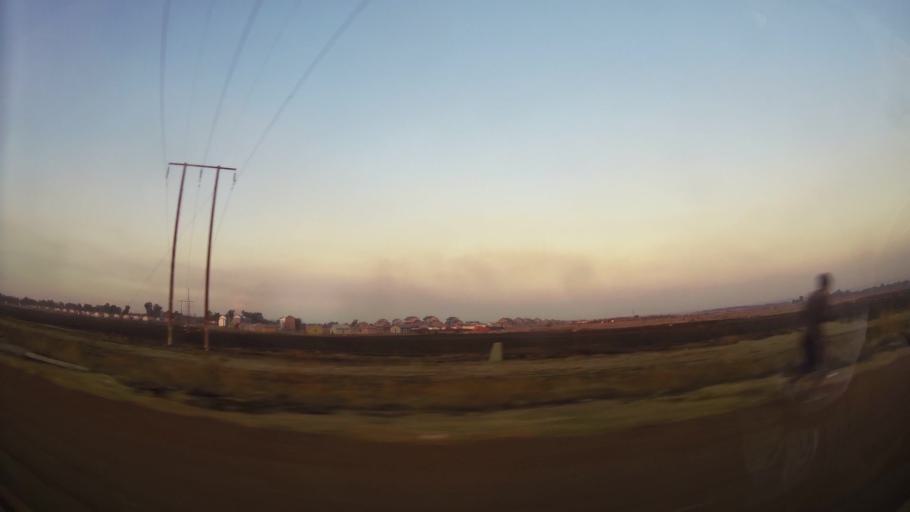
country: ZA
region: Gauteng
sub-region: Ekurhuleni Metropolitan Municipality
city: Springs
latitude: -26.3176
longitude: 28.4252
